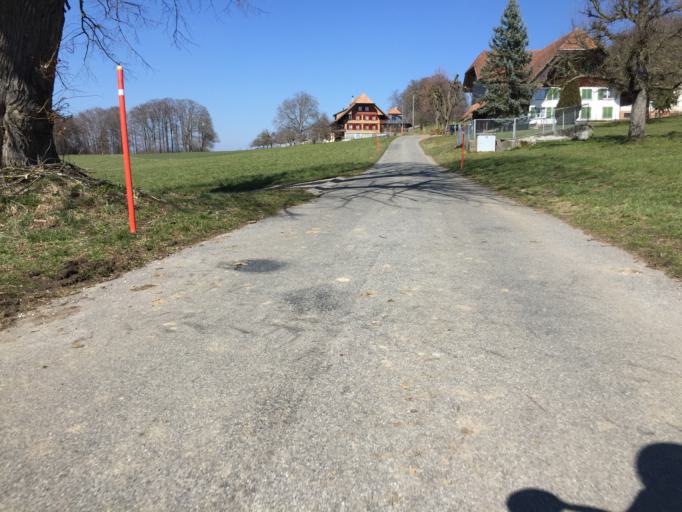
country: CH
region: Bern
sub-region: Bern-Mittelland District
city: Taegertschi
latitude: 46.8926
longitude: 7.5823
